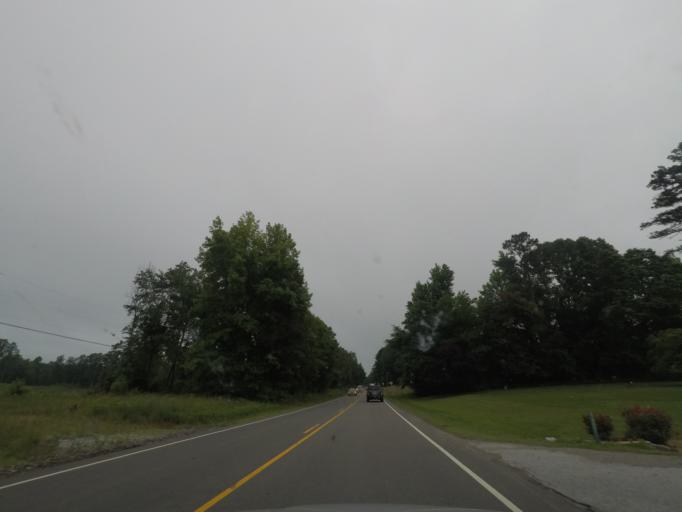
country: US
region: Virginia
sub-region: Prince Edward County
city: Hampden Sydney
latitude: 37.2391
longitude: -78.4438
